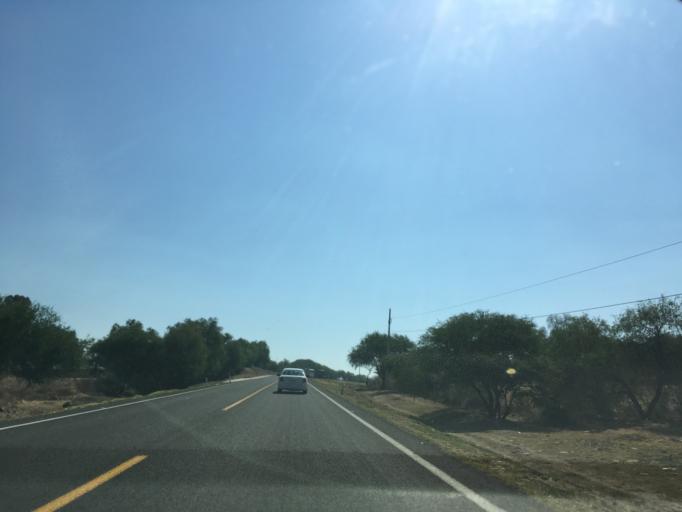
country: MX
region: Michoacan
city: Indaparapeo
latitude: 19.7837
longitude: -100.9994
